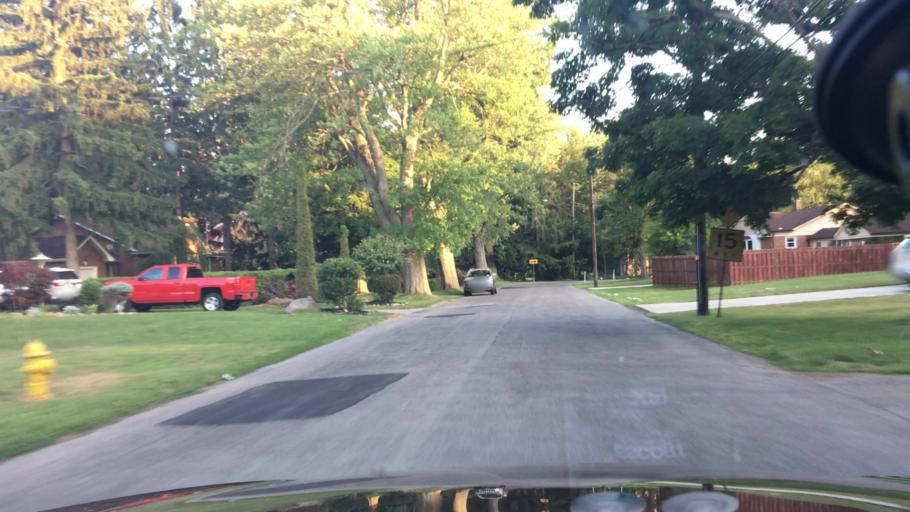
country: US
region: New York
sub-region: Erie County
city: West Seneca
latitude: 42.8280
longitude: -78.7506
